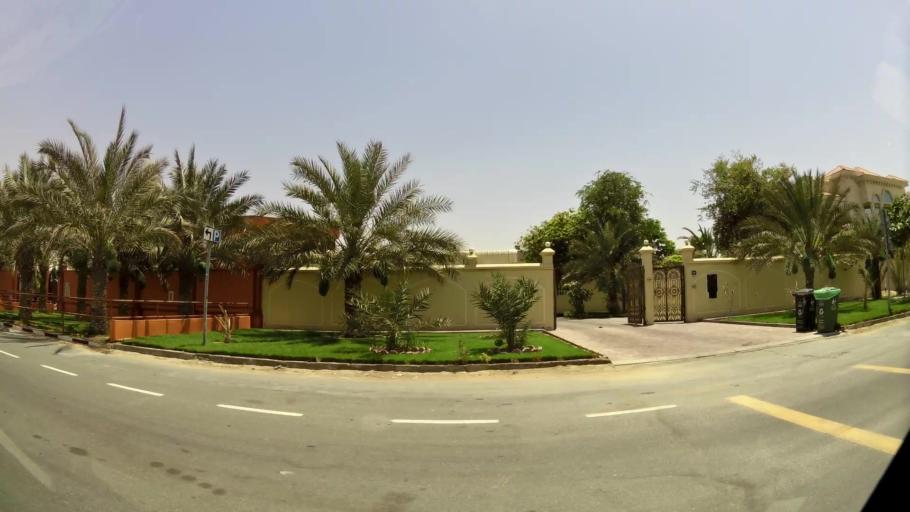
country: AE
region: Dubai
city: Dubai
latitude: 25.0864
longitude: 55.2035
